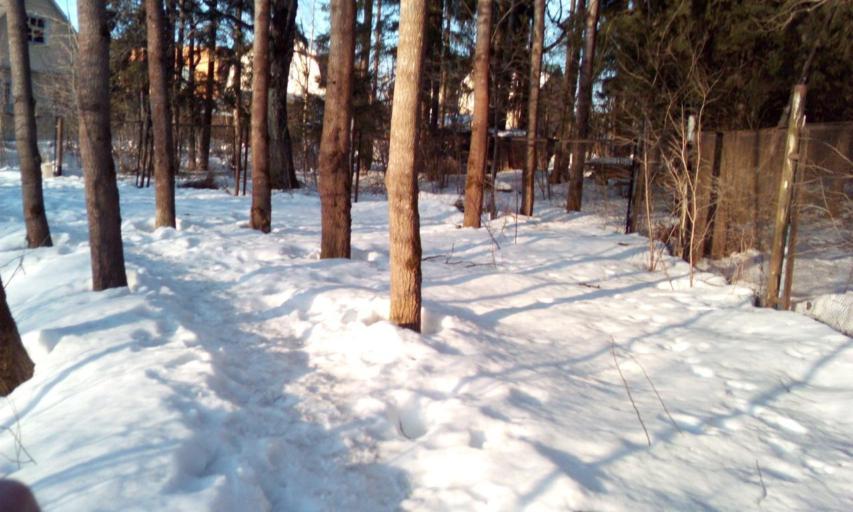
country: RU
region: Moscow
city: Tolstopal'tsevo
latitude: 55.6243
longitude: 37.2304
